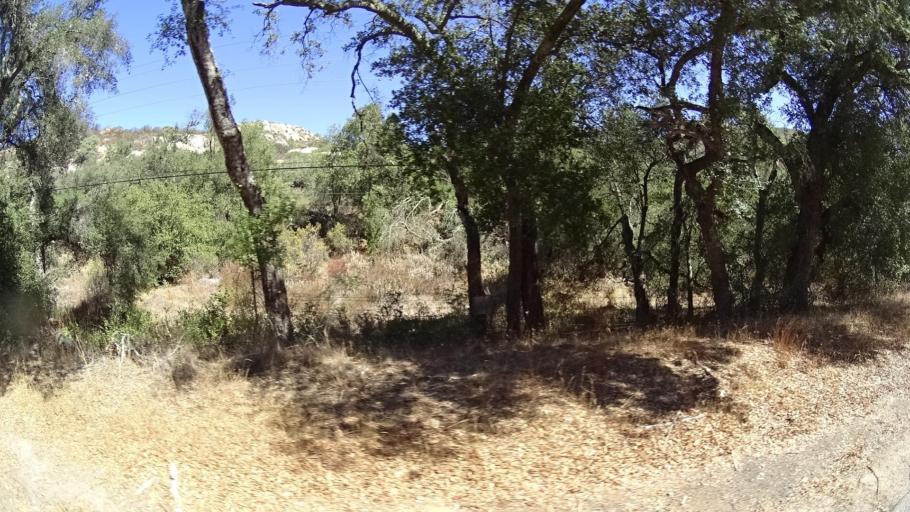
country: US
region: California
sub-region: San Diego County
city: Alpine
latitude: 32.7092
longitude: -116.7393
